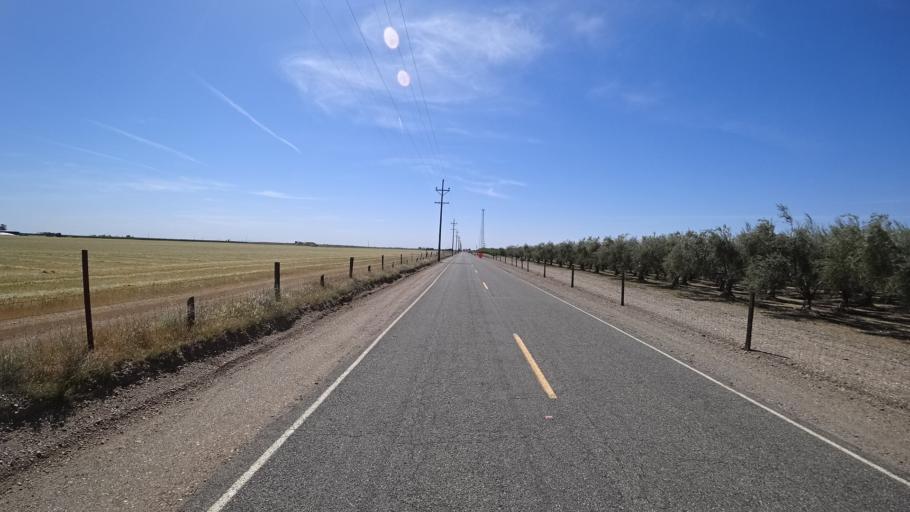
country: US
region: California
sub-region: Glenn County
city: Orland
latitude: 39.6577
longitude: -122.1785
